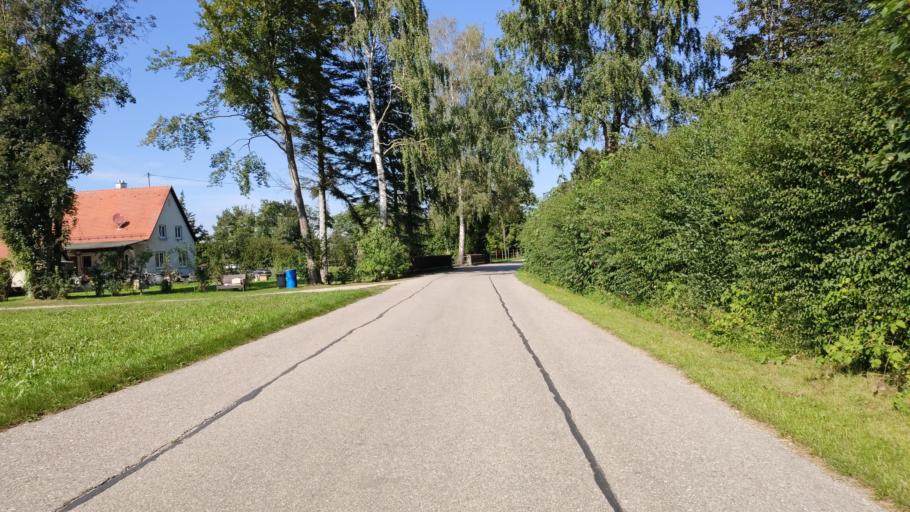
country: DE
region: Bavaria
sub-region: Swabia
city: Konigsbrunn
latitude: 48.2396
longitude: 10.9017
